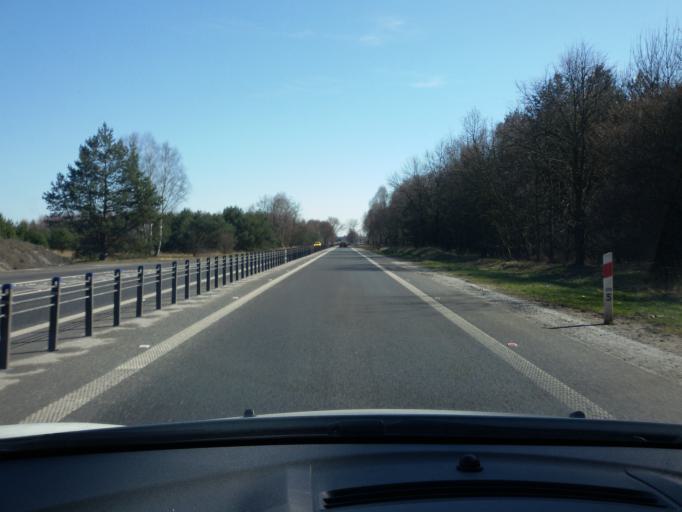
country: PL
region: Greater Poland Voivodeship
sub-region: Powiat leszczynski
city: Rydzyna
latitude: 51.8027
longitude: 16.6451
